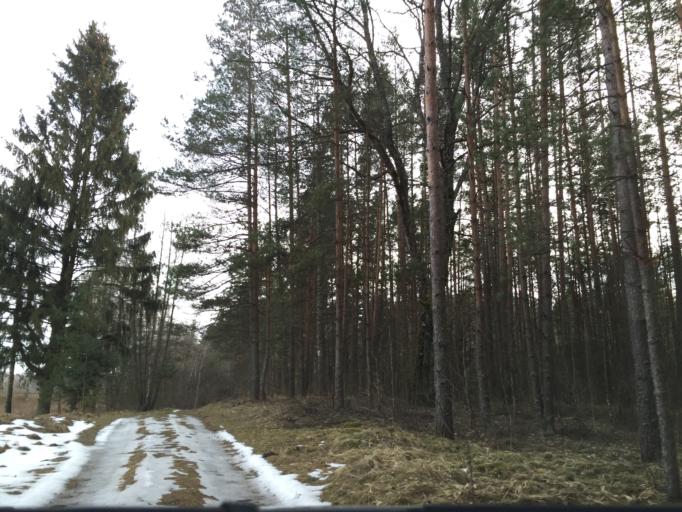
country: LV
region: Stopini
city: Ulbroka
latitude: 56.9220
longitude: 24.3057
